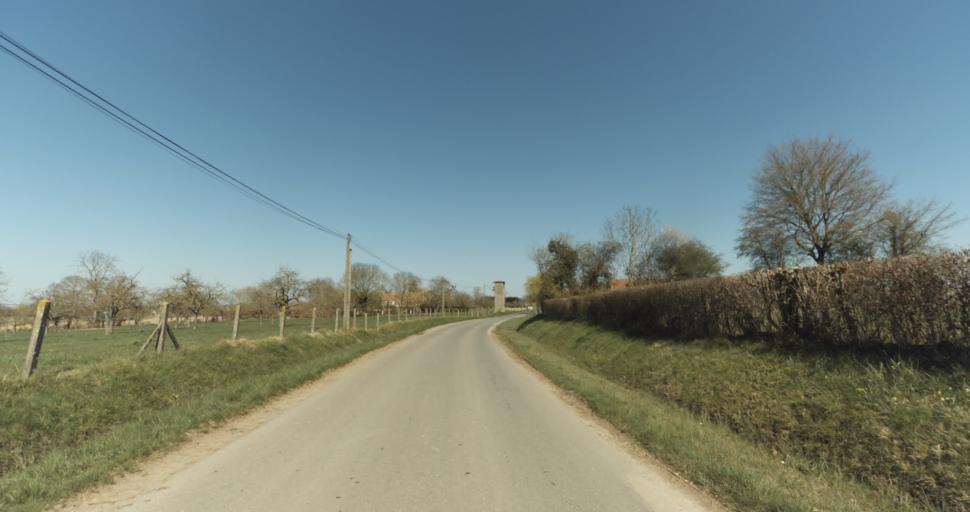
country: FR
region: Lower Normandy
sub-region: Departement du Calvados
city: Saint-Pierre-sur-Dives
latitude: 49.0143
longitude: -0.0069
